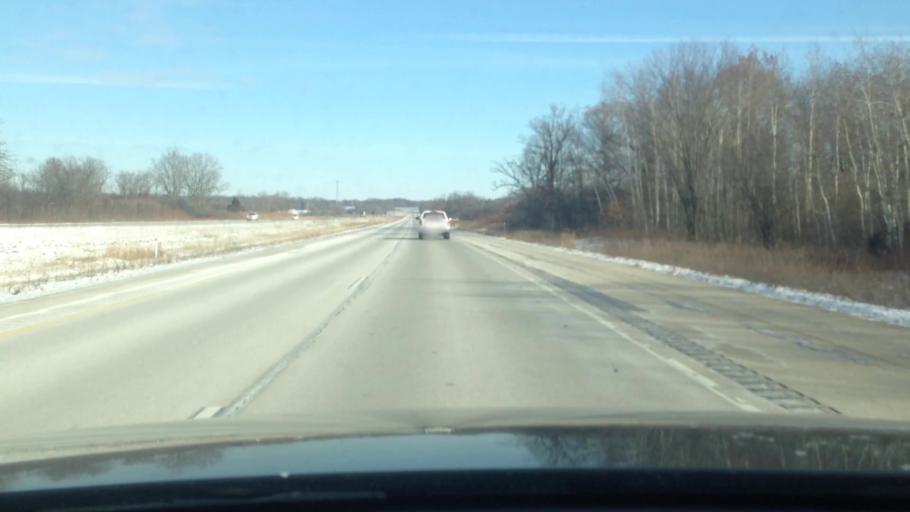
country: US
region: Wisconsin
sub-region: Walworth County
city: Potter Lake
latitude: 42.8092
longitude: -88.3683
